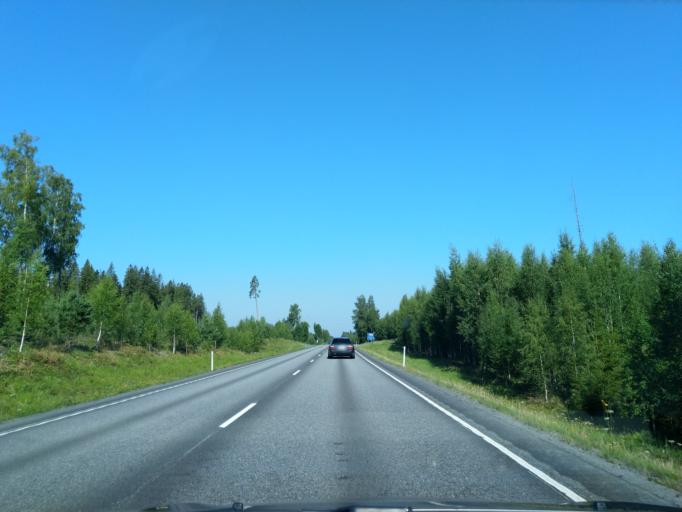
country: FI
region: Satakunta
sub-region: Pori
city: Huittinen
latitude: 61.1334
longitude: 22.7830
